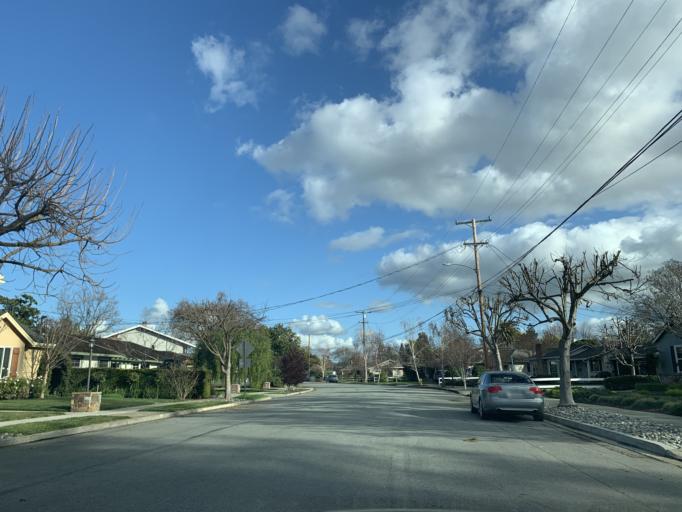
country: US
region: California
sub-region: Santa Clara County
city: Buena Vista
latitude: 37.3017
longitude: -121.9168
